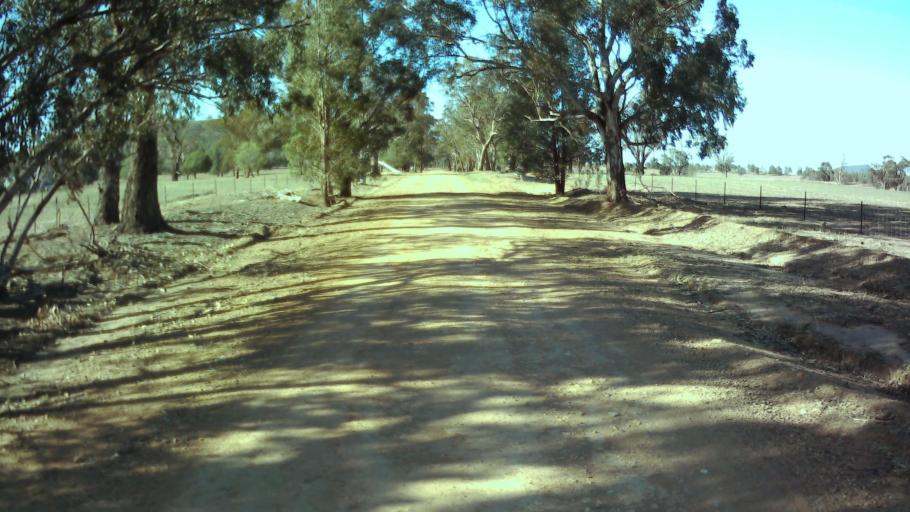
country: AU
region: New South Wales
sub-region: Weddin
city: Grenfell
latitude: -33.7961
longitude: 147.8800
